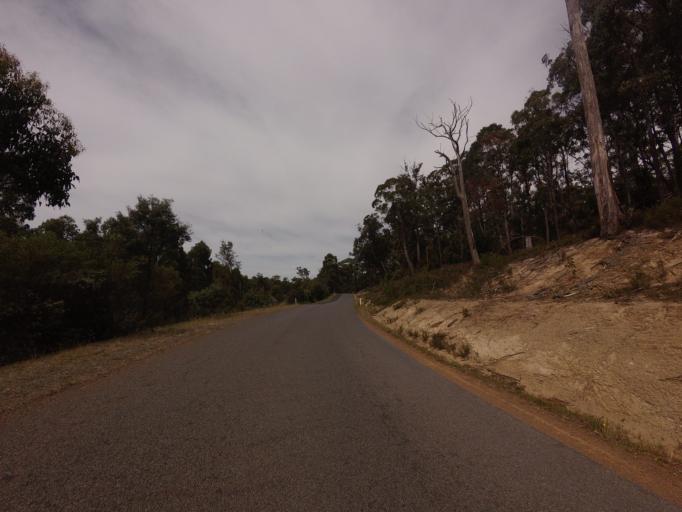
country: AU
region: Tasmania
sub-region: Sorell
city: Sorell
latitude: -42.5854
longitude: 147.5586
